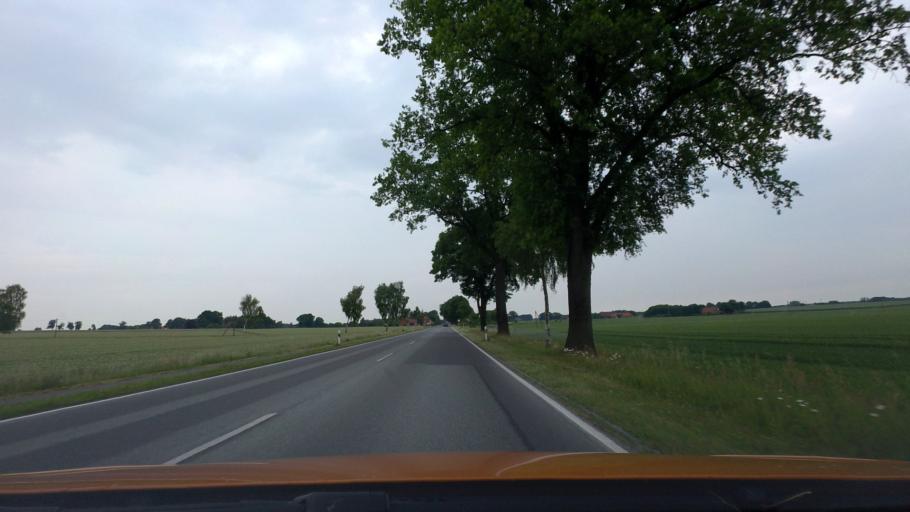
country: DE
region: Lower Saxony
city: Asendorf
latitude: 52.7456
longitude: 9.0218
